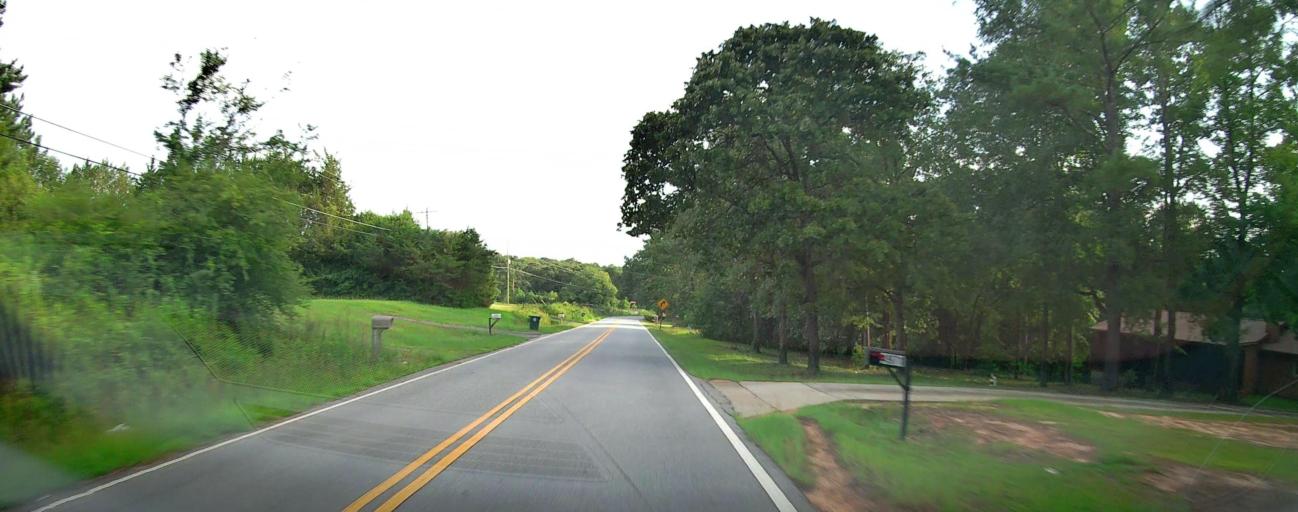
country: US
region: Georgia
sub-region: Peach County
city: Byron
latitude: 32.7385
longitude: -83.7328
